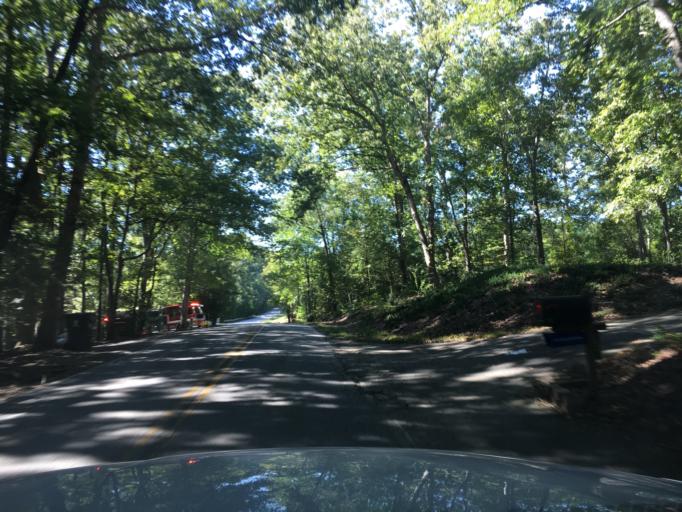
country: US
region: South Carolina
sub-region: Greenville County
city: Taylors
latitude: 34.8963
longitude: -82.2745
